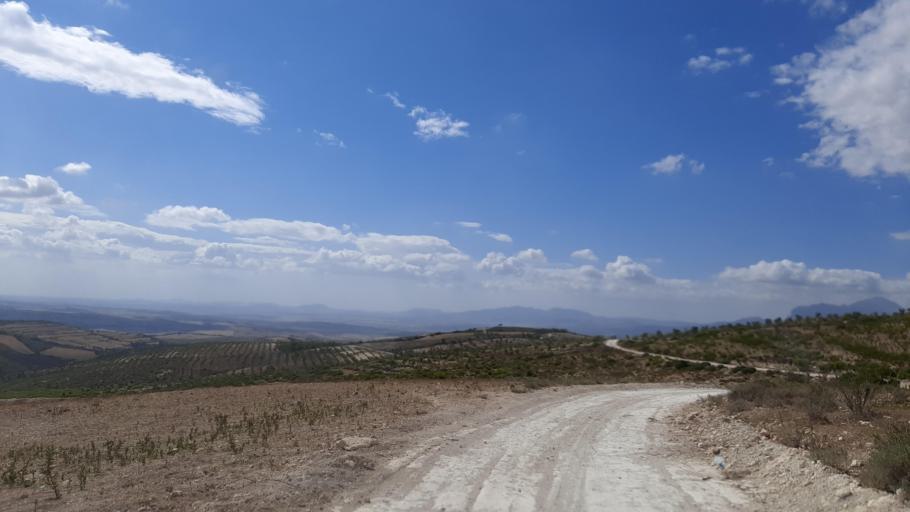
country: TN
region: Zaghwan
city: Zaghouan
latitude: 36.5062
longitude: 10.1846
